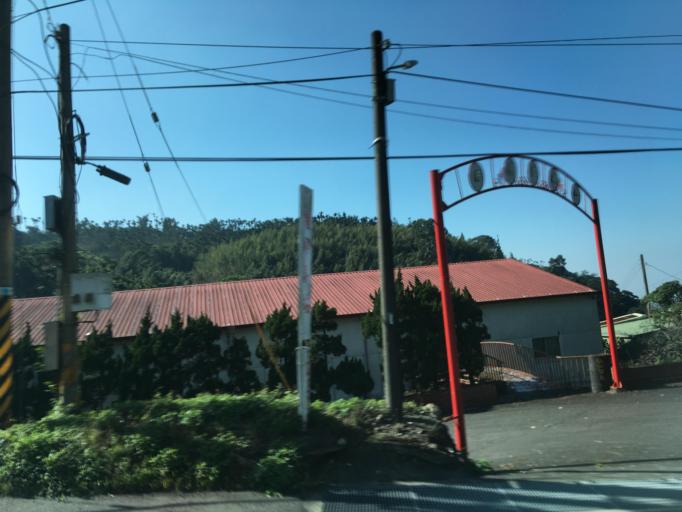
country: TW
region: Taiwan
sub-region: Chiayi
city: Jiayi Shi
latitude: 23.4195
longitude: 120.6435
